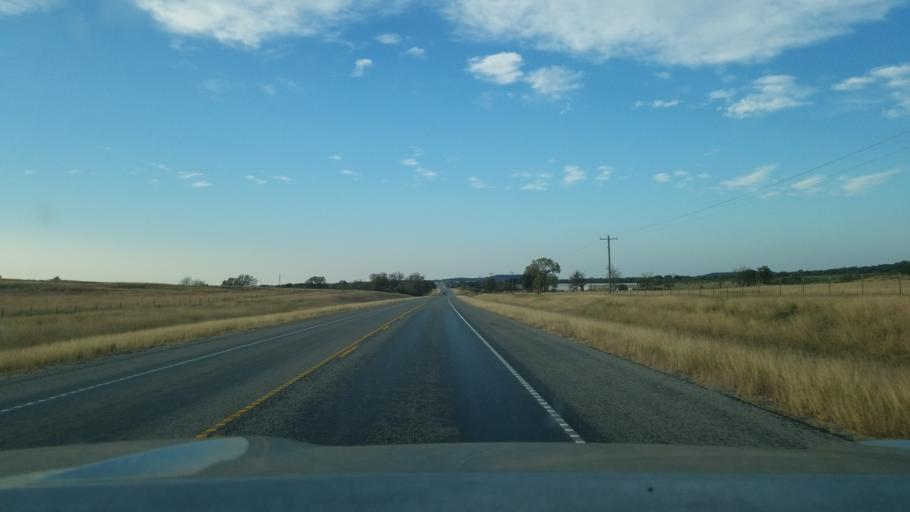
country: US
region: Texas
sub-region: Brown County
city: Lake Brownwood
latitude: 32.0345
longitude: -98.9346
